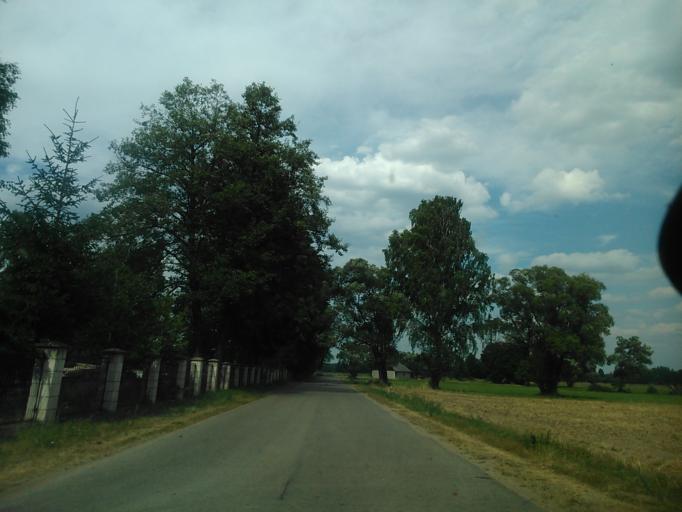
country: PL
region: Masovian Voivodeship
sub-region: Powiat ostrolecki
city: Czarnia
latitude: 53.3587
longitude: 21.1936
